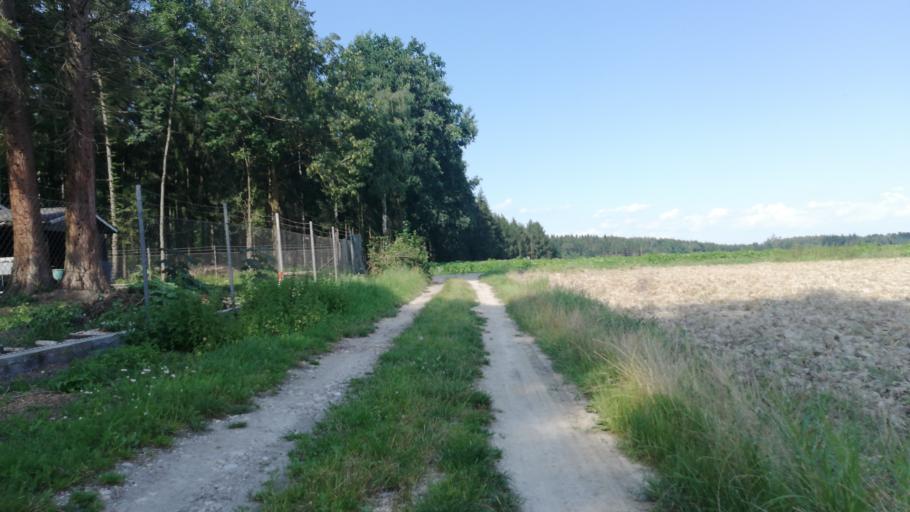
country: AT
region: Upper Austria
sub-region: Wels-Land
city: Gunskirchen
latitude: 48.1689
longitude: 13.9259
